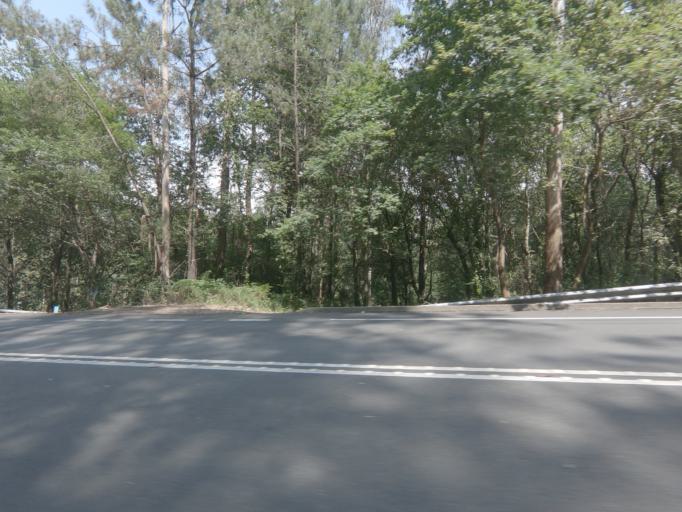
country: ES
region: Galicia
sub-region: Provincia de Pontevedra
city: Gondomar
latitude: 42.0832
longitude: -8.7508
